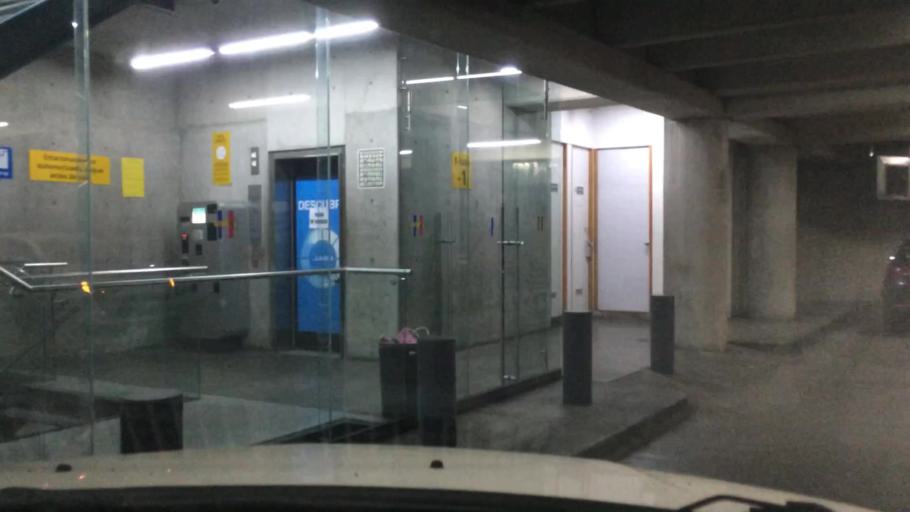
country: MX
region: Mexico City
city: Alvaro Obregon
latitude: 19.3412
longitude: -99.1894
